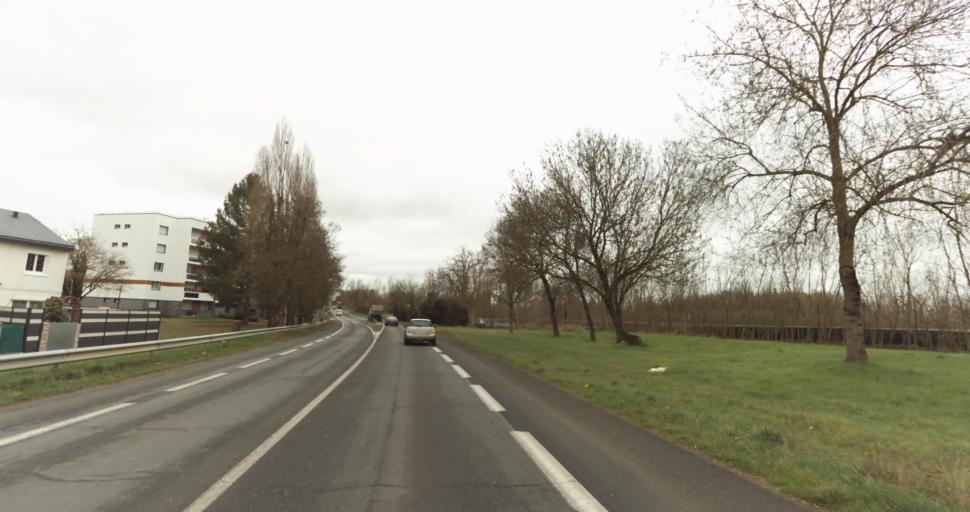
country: FR
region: Pays de la Loire
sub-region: Departement de Maine-et-Loire
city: Varrains
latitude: 47.2392
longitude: -0.0792
